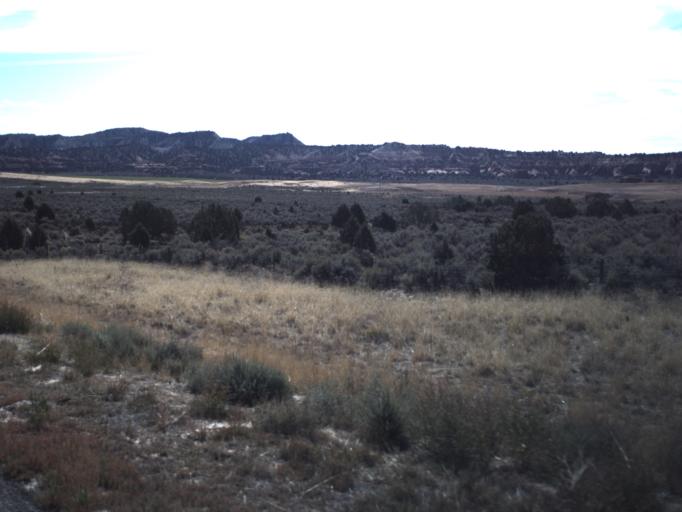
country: US
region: Utah
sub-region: Garfield County
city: Panguitch
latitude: 37.5631
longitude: -112.0340
